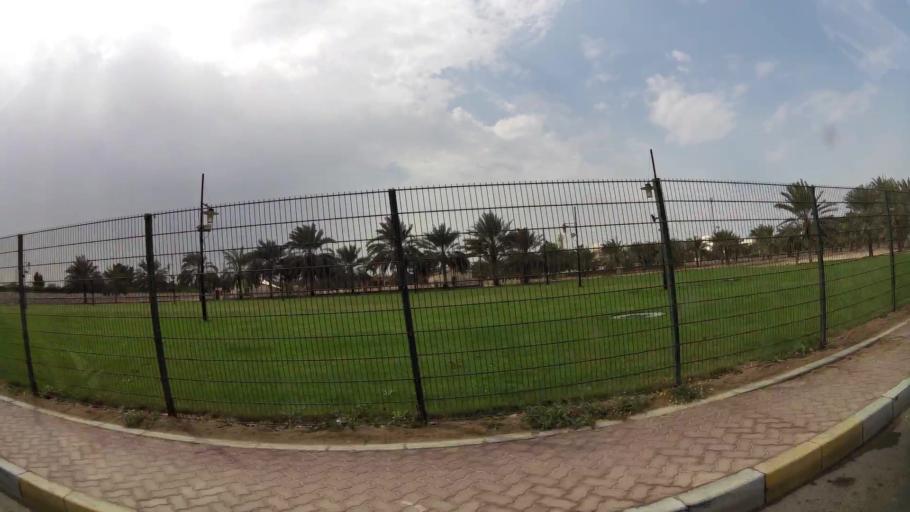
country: AE
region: Abu Dhabi
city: Abu Dhabi
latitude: 24.4275
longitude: 54.4708
